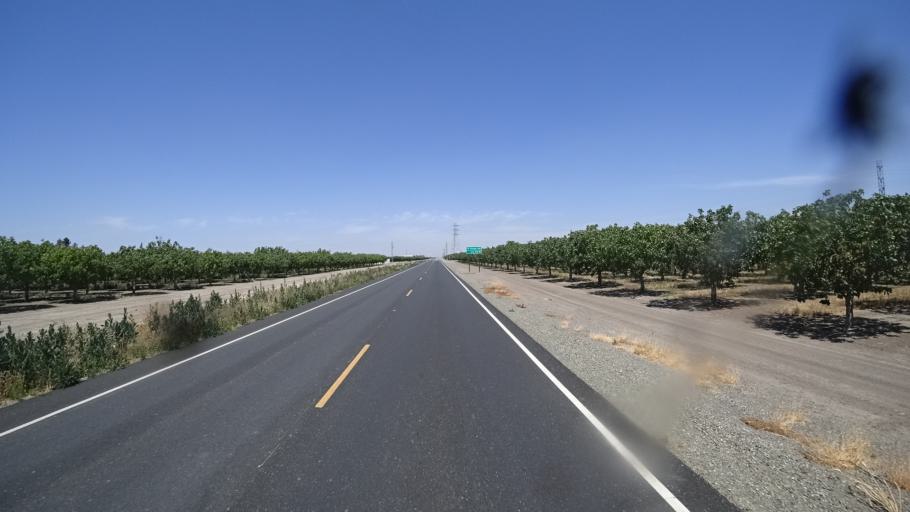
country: US
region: California
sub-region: Kings County
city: Corcoran
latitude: 36.1067
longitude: -119.5365
